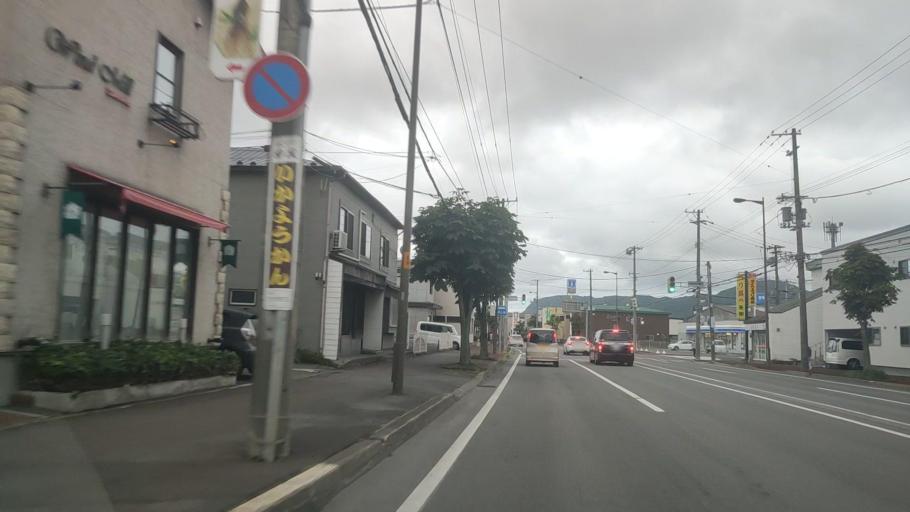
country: JP
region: Hokkaido
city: Hakodate
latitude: 41.7871
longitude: 140.7309
